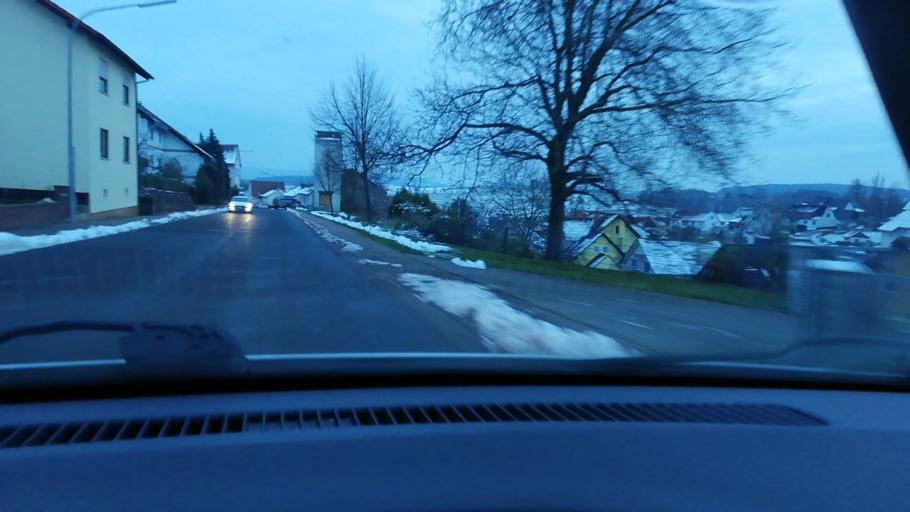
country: DE
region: Bavaria
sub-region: Regierungsbezirk Unterfranken
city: Geiselbach
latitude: 50.1247
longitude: 9.1918
